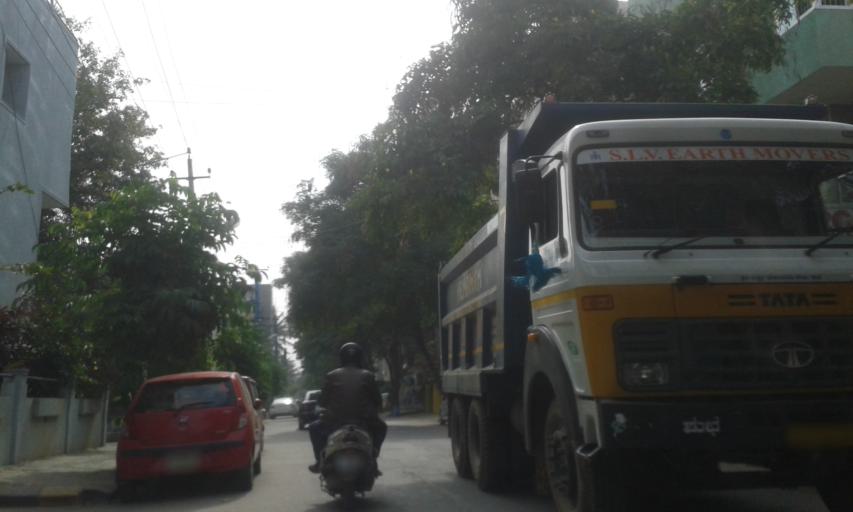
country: IN
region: Karnataka
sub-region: Bangalore Urban
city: Bangalore
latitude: 12.9344
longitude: 77.6307
